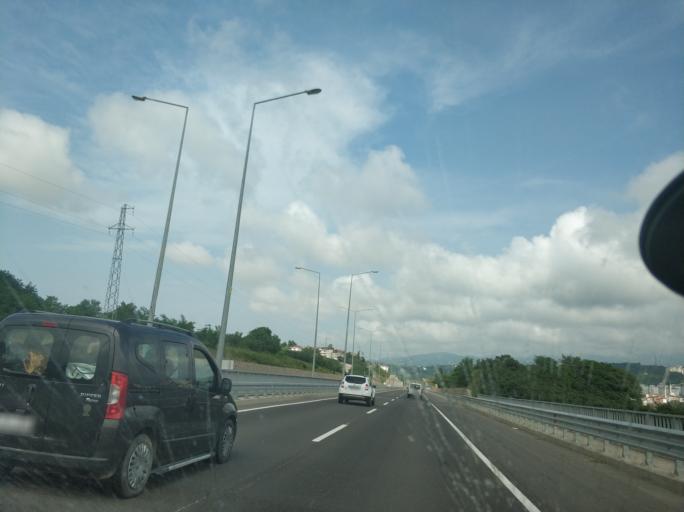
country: TR
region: Ordu
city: Ordu
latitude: 40.9554
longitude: 37.8766
